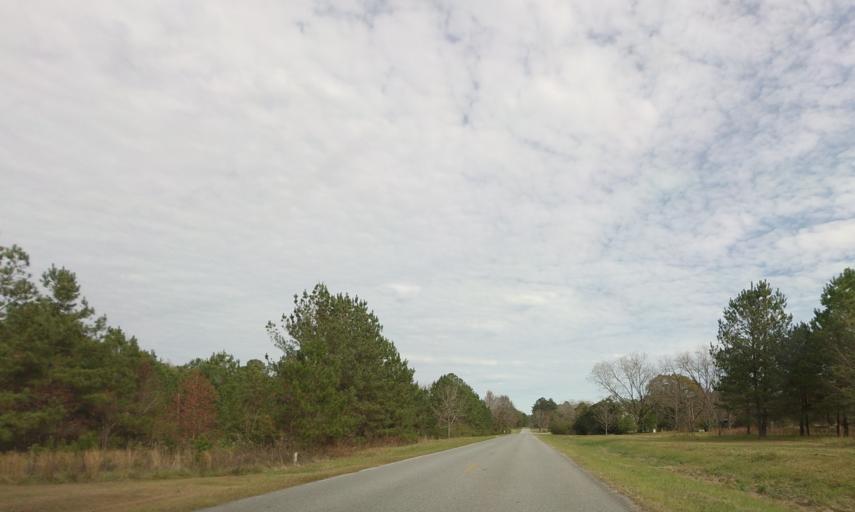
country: US
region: Georgia
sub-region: Dodge County
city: Chester
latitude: 32.4584
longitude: -83.1323
